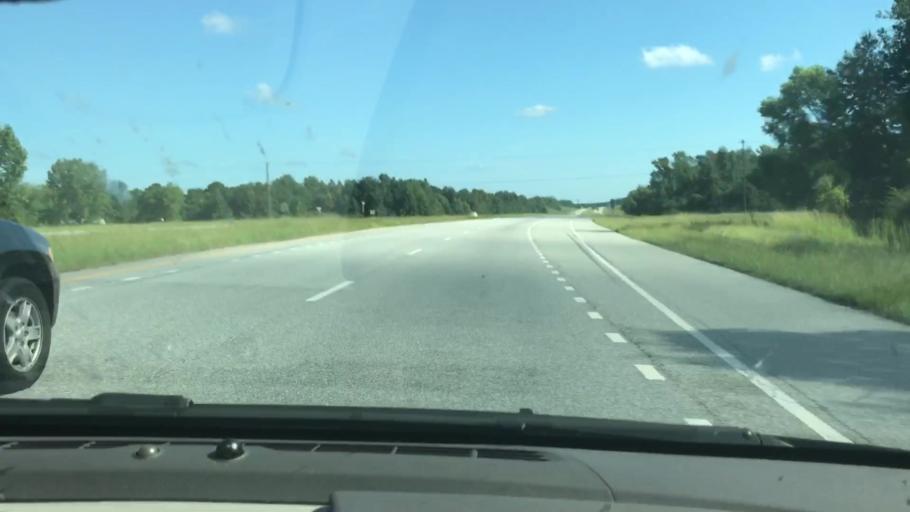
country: US
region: Alabama
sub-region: Russell County
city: Ladonia
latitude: 32.1936
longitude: -85.1806
